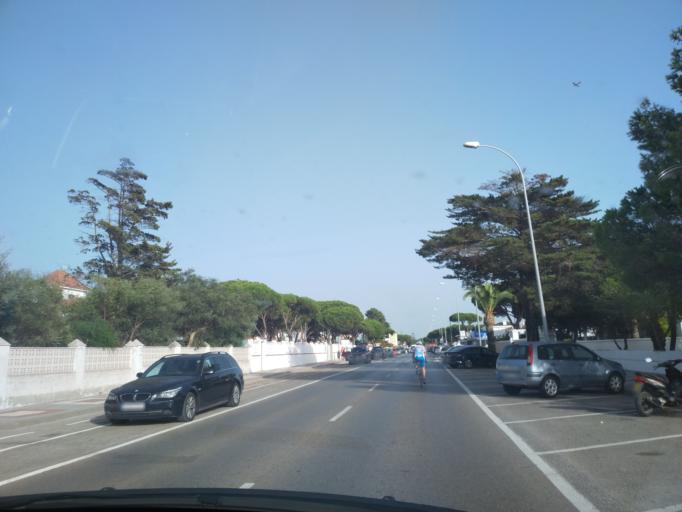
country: ES
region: Andalusia
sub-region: Provincia de Cadiz
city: Chiclana de la Frontera
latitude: 36.3734
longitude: -6.1834
